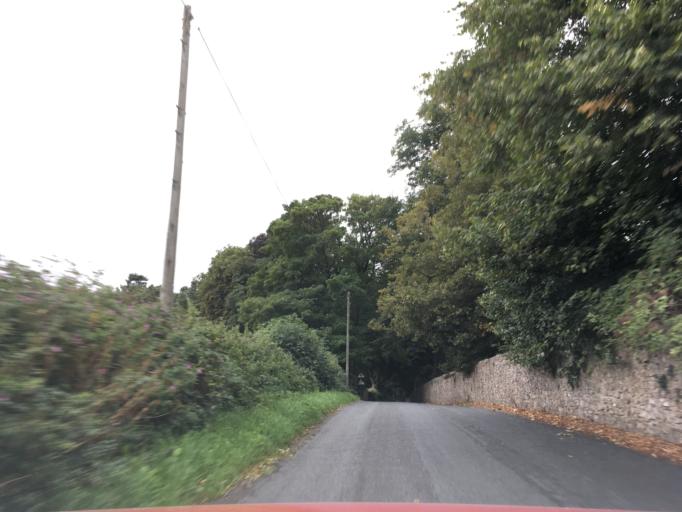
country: GB
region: Wales
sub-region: Monmouthshire
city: Chepstow
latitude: 51.6252
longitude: -2.6865
